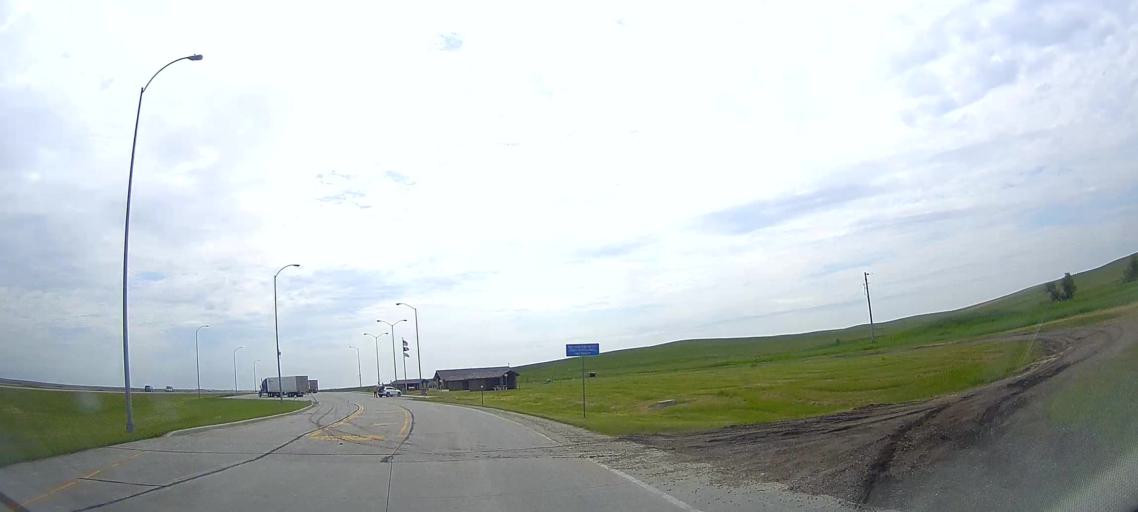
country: US
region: South Dakota
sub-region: Lyman County
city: Kennebec
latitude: 43.9118
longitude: -100.2014
